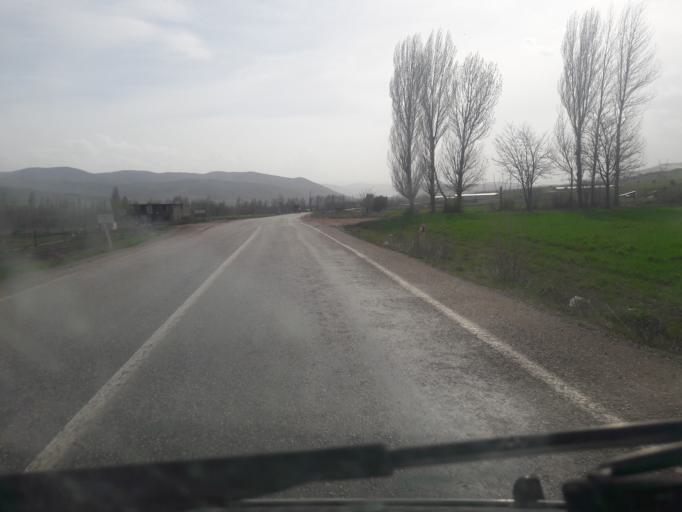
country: TR
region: Gumushane
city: Kelkit
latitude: 40.1336
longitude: 39.3760
